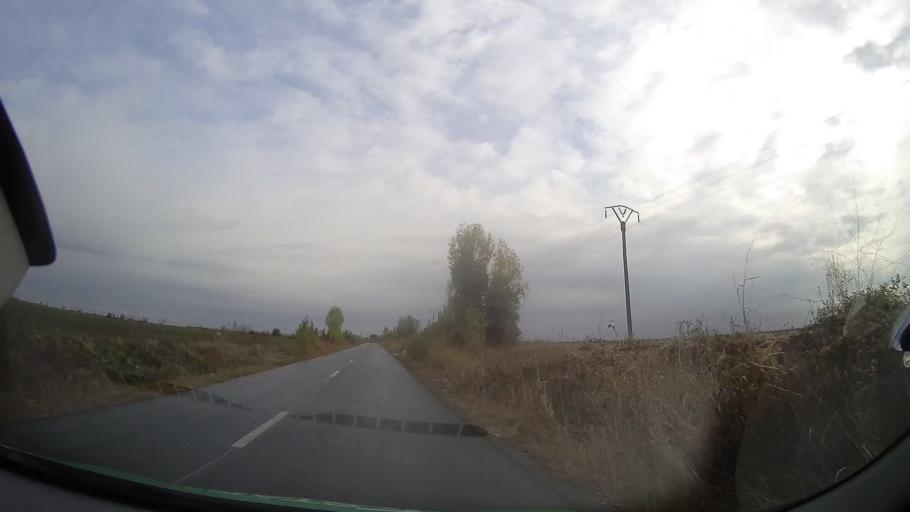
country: RO
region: Ialomita
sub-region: Comuna Maia
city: Maia
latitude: 44.7510
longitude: 26.3898
